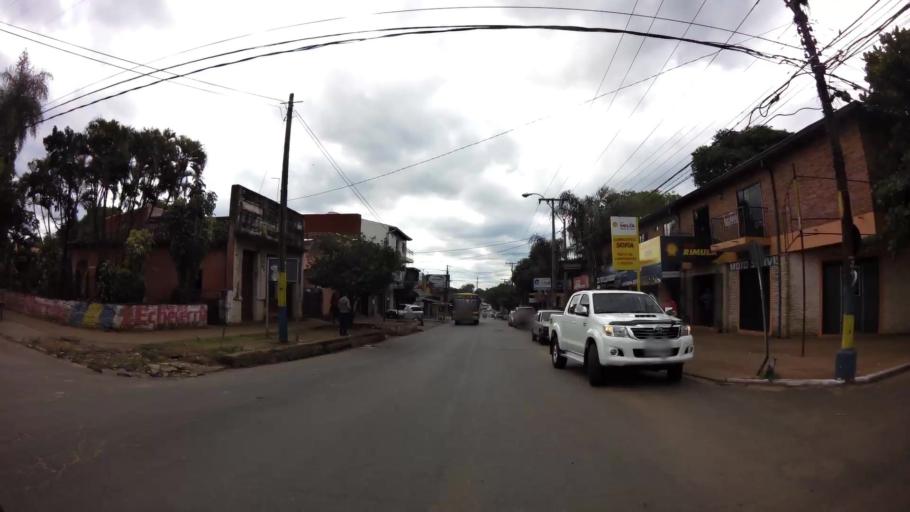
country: PY
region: Central
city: San Lorenzo
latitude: -25.2713
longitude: -57.4935
